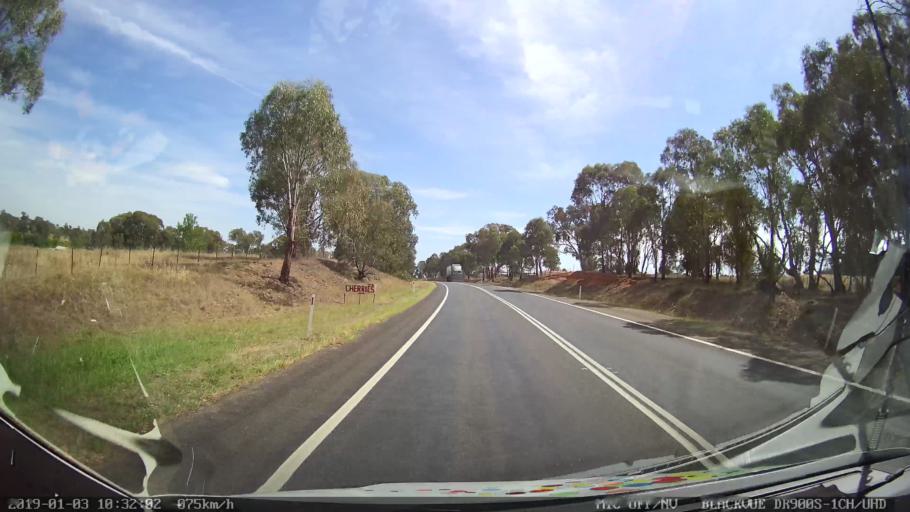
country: AU
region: New South Wales
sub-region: Young
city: Young
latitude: -34.3434
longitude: 148.2824
